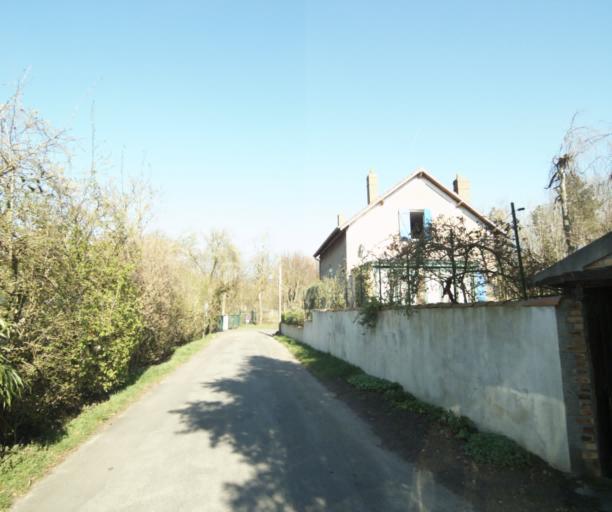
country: FR
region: Ile-de-France
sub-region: Departement du Val-d'Oise
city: Neuville-sur-Oise
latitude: 49.0285
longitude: 2.0566
